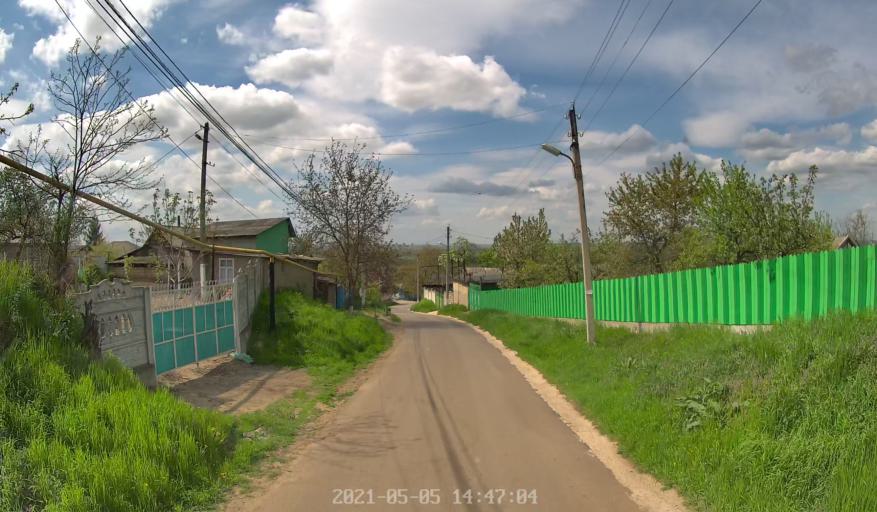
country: MD
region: Chisinau
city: Vadul lui Voda
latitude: 47.0961
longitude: 29.1710
